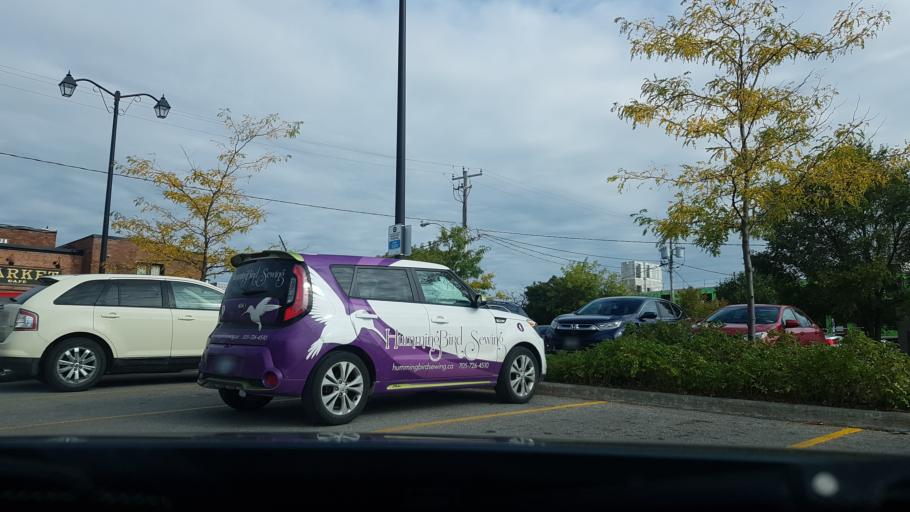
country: CA
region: Ontario
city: Orillia
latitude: 44.6087
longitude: -79.4165
